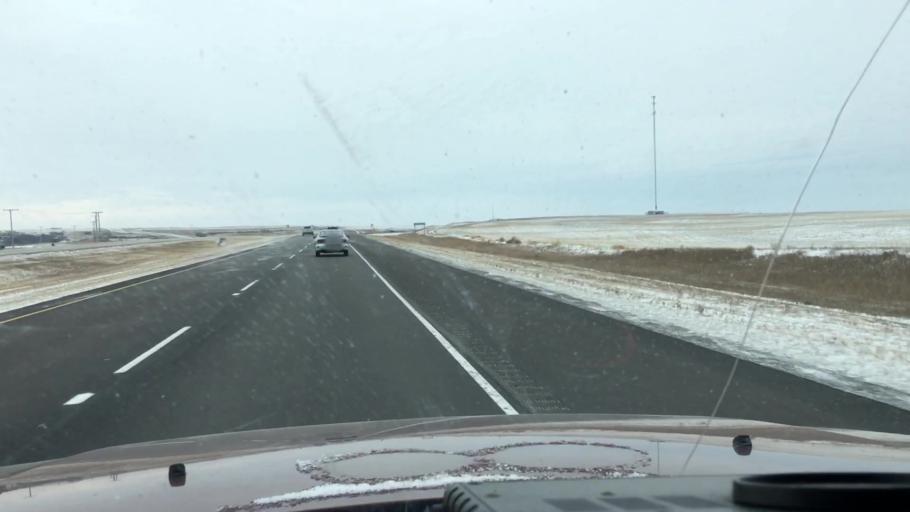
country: CA
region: Saskatchewan
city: Saskatoon
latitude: 51.7425
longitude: -106.4763
